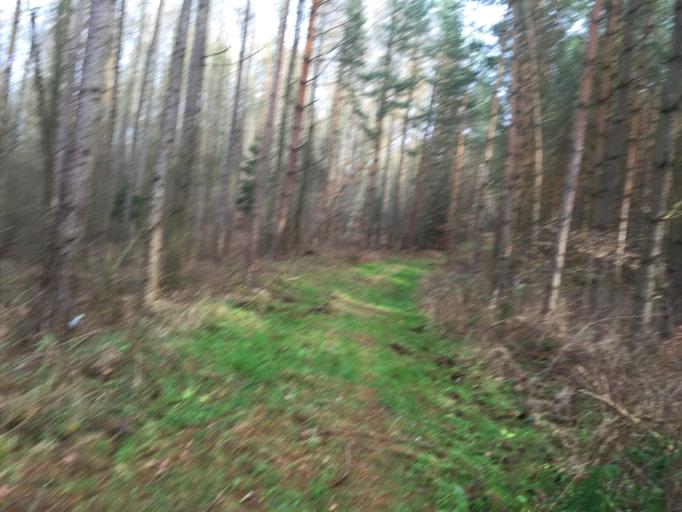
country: DE
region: Thuringia
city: Bollberg
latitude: 50.8866
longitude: 11.7825
